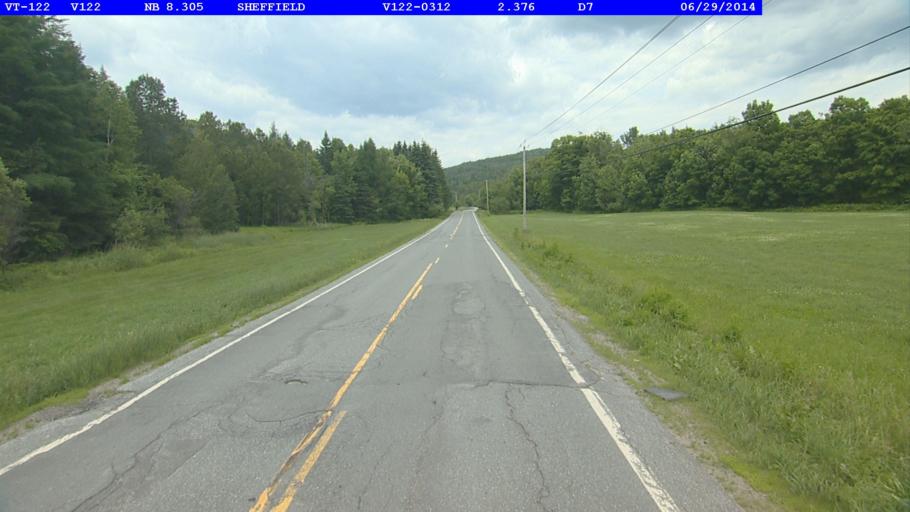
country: US
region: Vermont
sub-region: Caledonia County
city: Lyndonville
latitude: 44.6138
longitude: -72.1227
